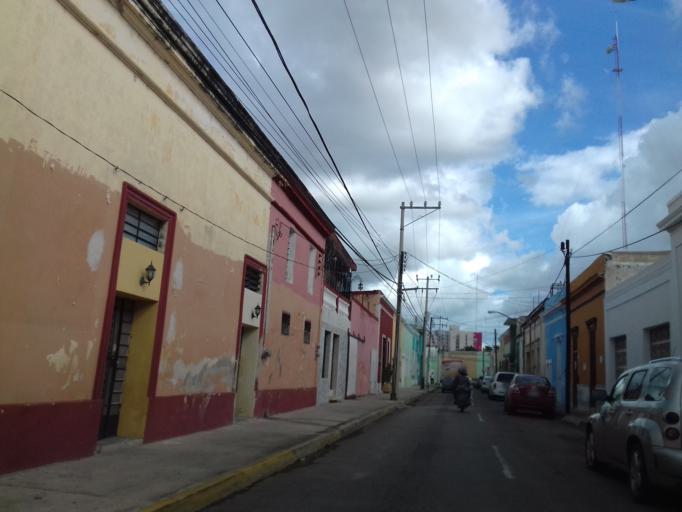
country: MX
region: Yucatan
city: Merida
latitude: 20.9721
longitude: -89.6296
